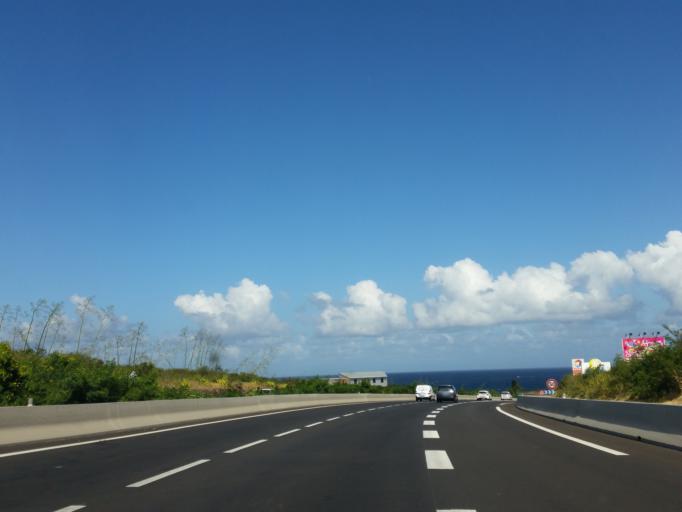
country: RE
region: Reunion
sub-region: Reunion
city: Saint-Pierre
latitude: -21.3199
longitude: 55.4460
